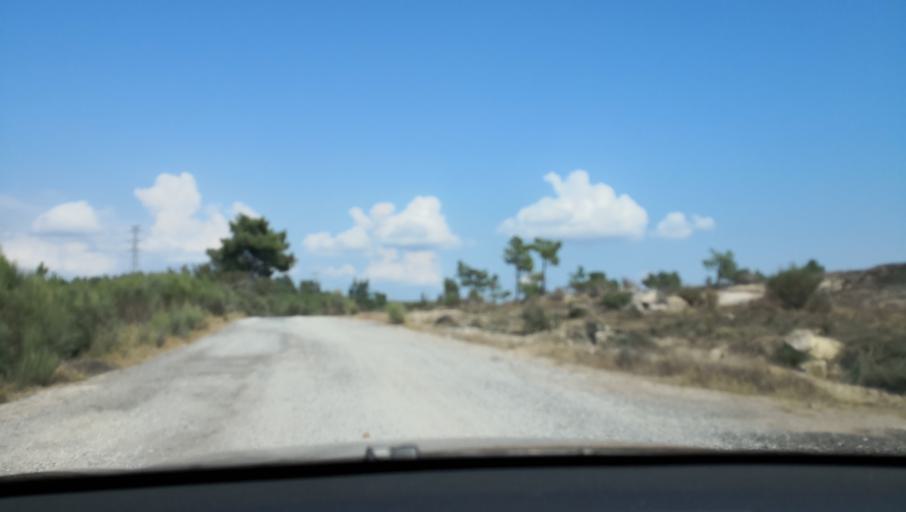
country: PT
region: Vila Real
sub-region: Sabrosa
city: Sabrosa
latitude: 41.3183
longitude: -7.6202
